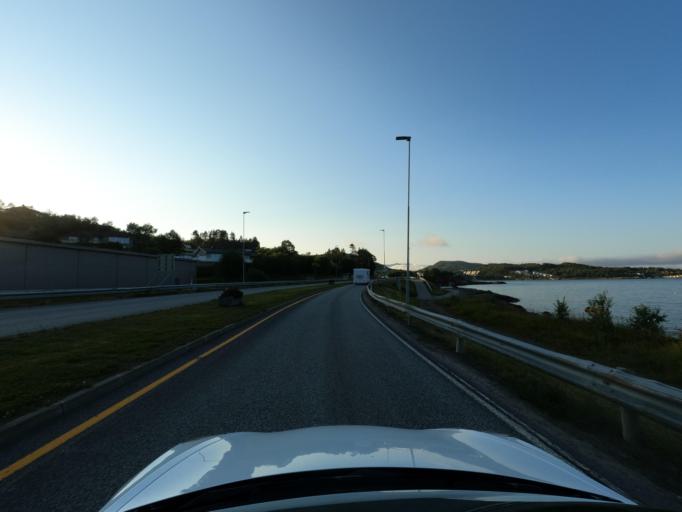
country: NO
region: Troms
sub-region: Harstad
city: Harstad
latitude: 68.7627
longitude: 16.5607
